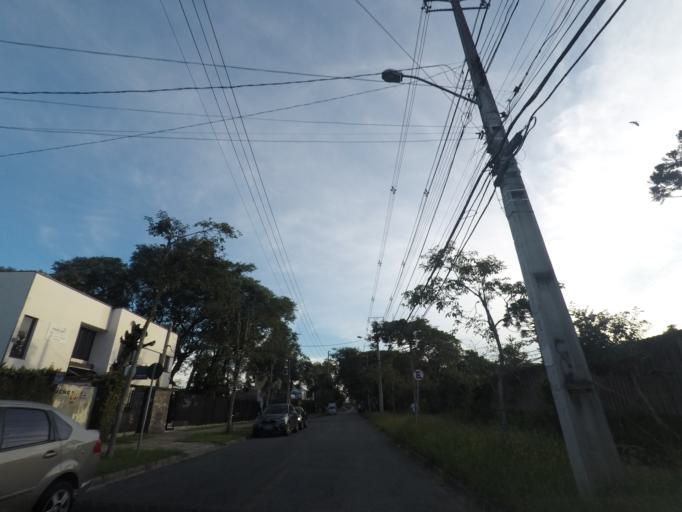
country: BR
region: Parana
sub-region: Curitiba
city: Curitiba
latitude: -25.4156
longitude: -49.2487
